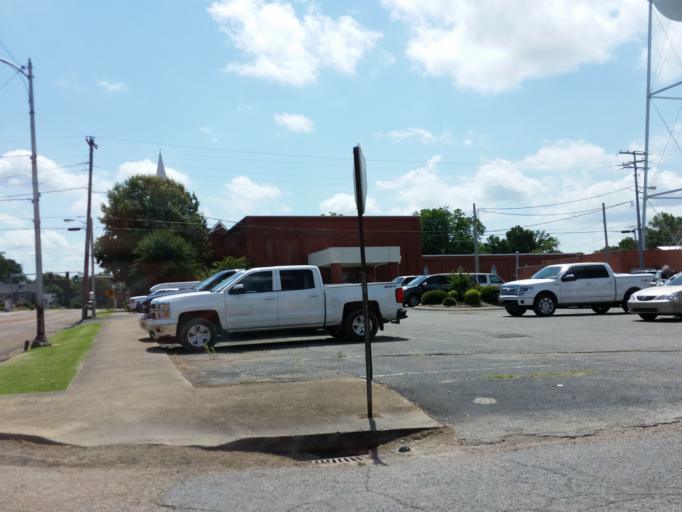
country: US
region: Tennessee
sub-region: Weakley County
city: Martin
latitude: 36.3429
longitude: -88.8490
